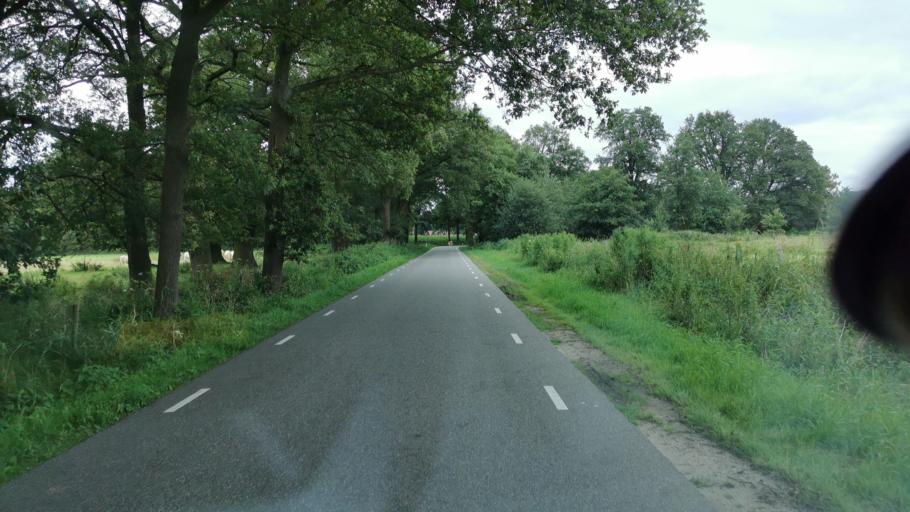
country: NL
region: Overijssel
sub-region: Gemeente Losser
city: Losser
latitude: 52.2387
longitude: 6.9509
